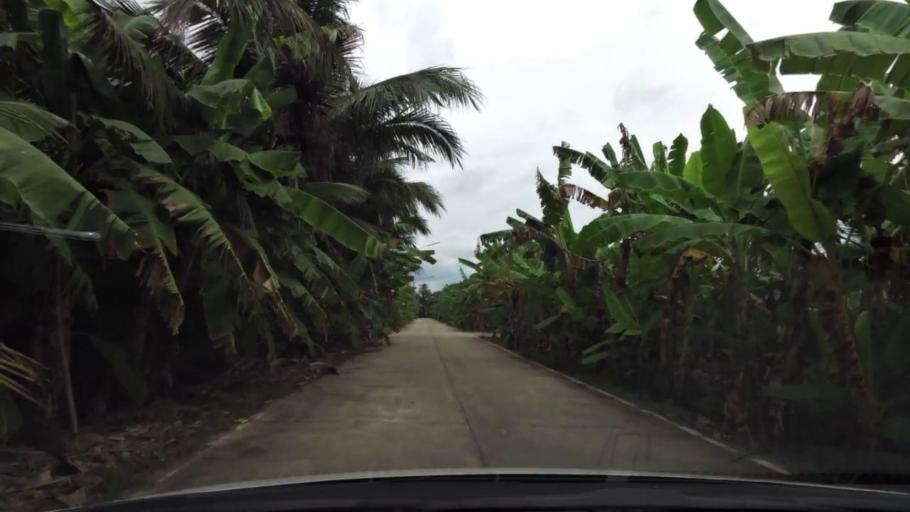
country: TH
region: Ratchaburi
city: Damnoen Saduak
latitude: 13.5506
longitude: 100.0205
